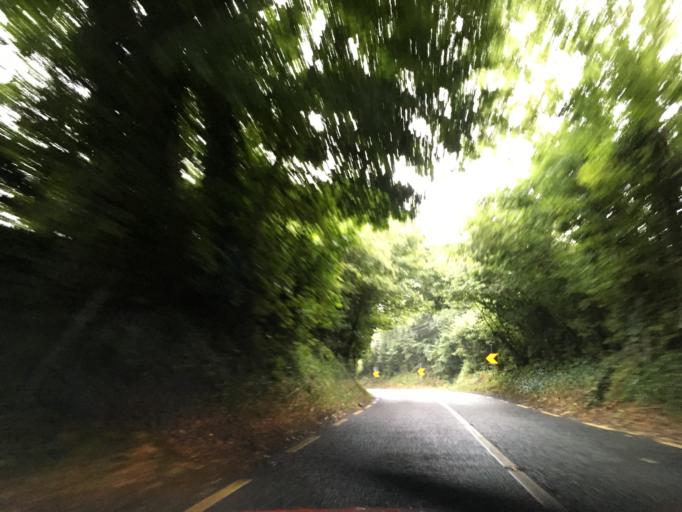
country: IE
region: Munster
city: Tipperary
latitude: 52.4797
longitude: -8.1244
